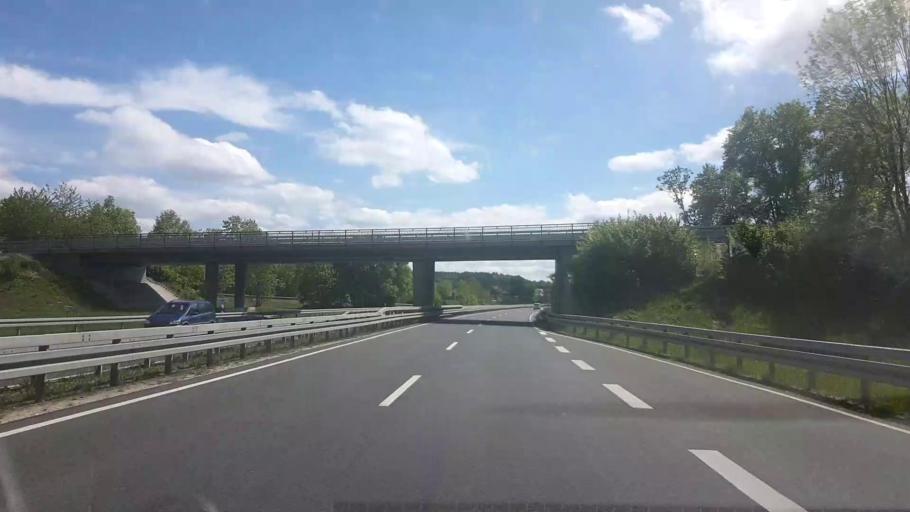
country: DE
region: Bavaria
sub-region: Upper Franconia
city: Niederfullbach
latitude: 50.2238
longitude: 10.9809
